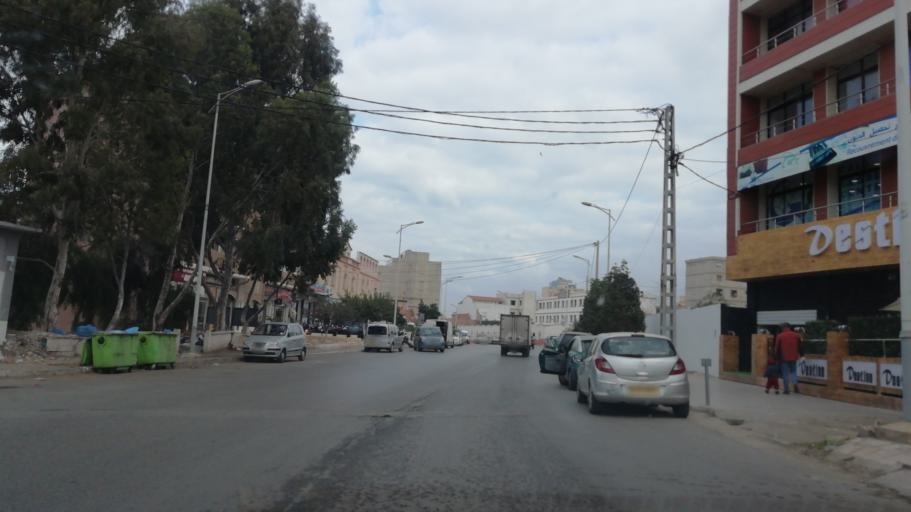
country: DZ
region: Oran
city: Oran
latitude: 35.7083
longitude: -0.6110
